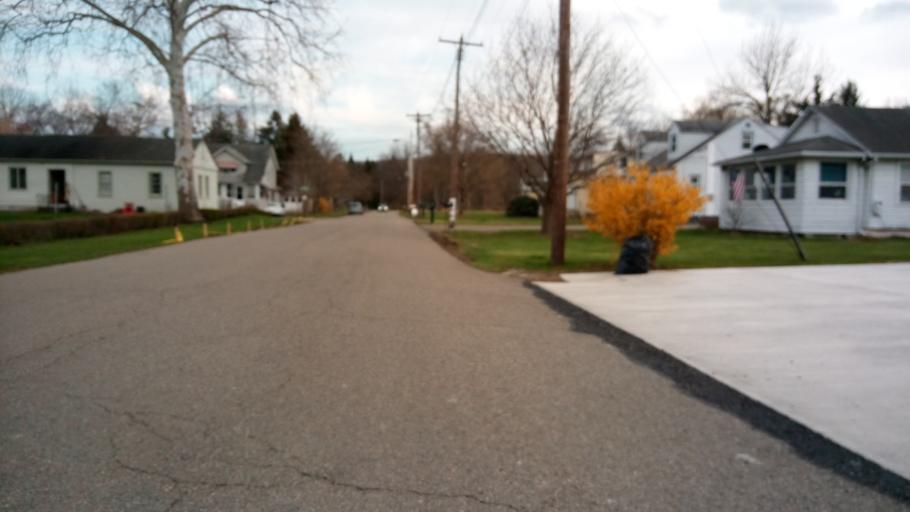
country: US
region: New York
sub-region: Chemung County
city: Southport
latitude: 42.0694
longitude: -76.8180
